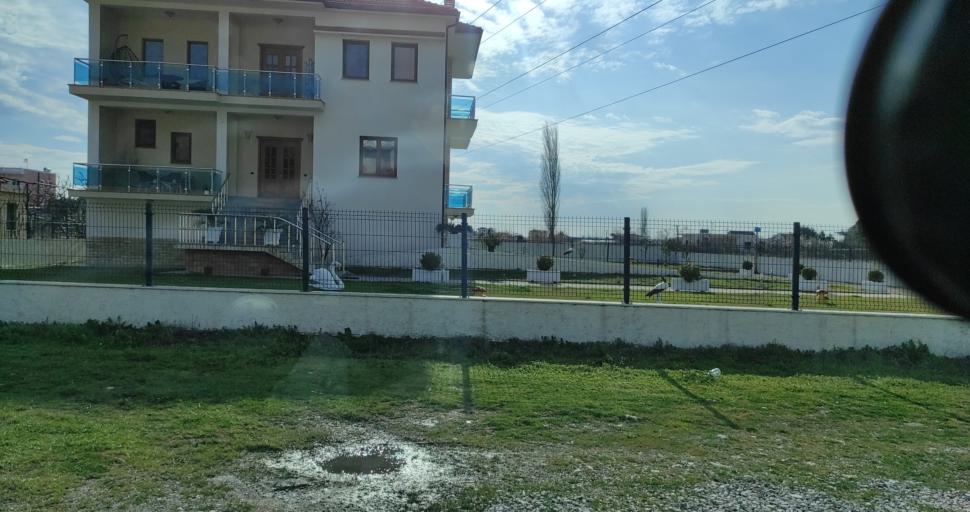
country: AL
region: Lezhe
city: Lezhe
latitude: 41.7849
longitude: 19.6285
